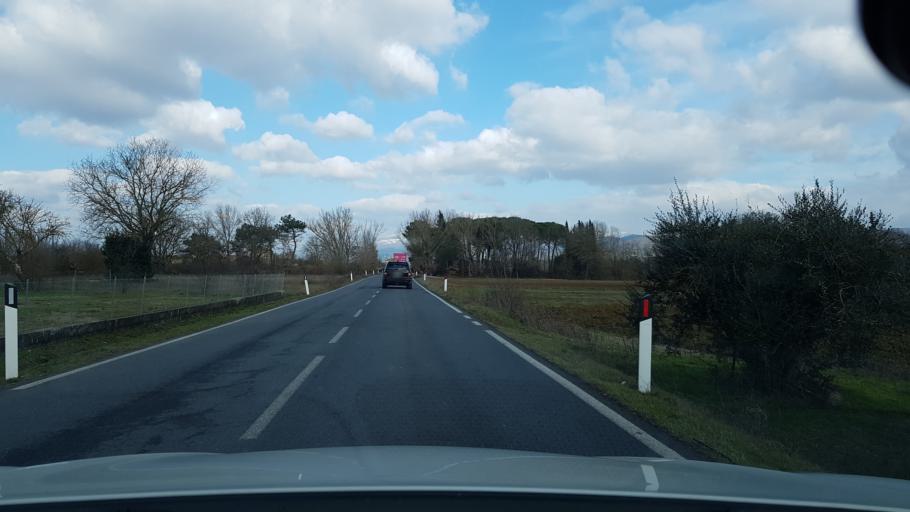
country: IT
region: Tuscany
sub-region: Province of Arezzo
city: Terontola
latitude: 43.1690
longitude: 12.0144
